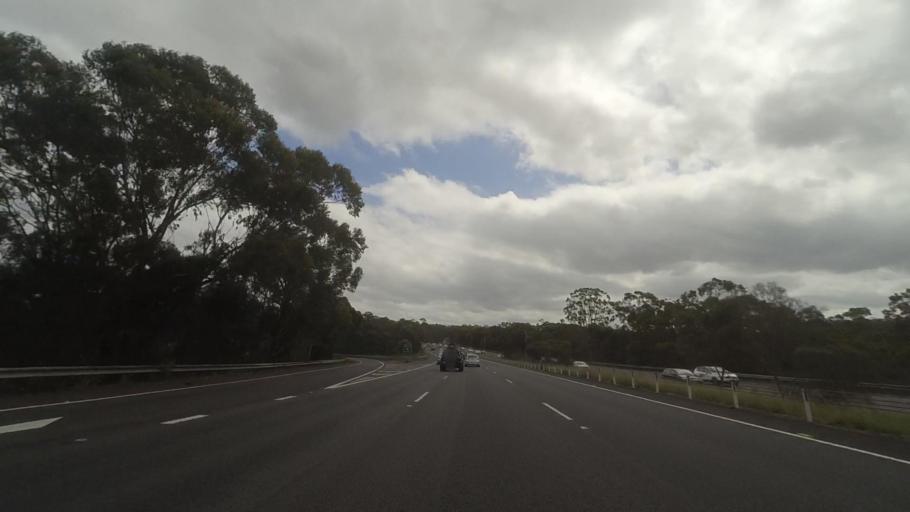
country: AU
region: New South Wales
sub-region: Gosford Shire
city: Point Clare
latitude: -33.4603
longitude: 151.1992
